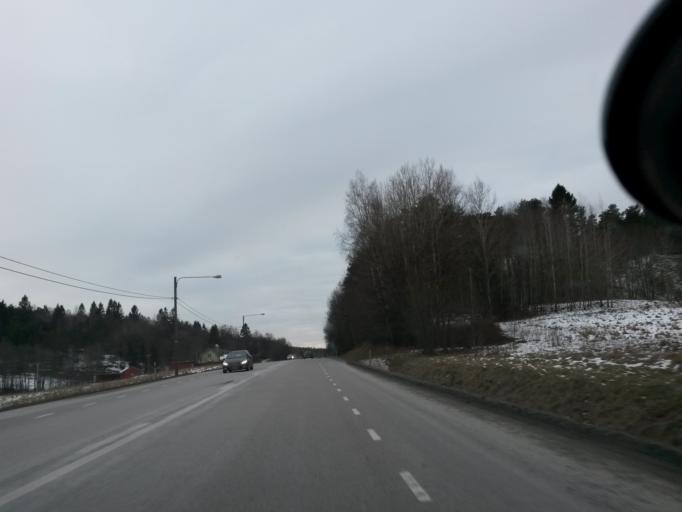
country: SE
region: Vaestra Goetaland
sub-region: Alingsas Kommun
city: Alingsas
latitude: 57.9462
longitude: 12.5970
